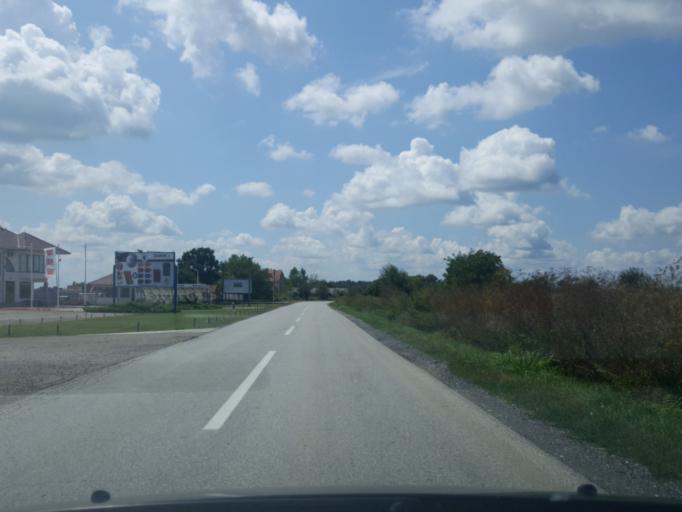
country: RS
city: Metkovic
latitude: 44.8430
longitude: 19.5170
